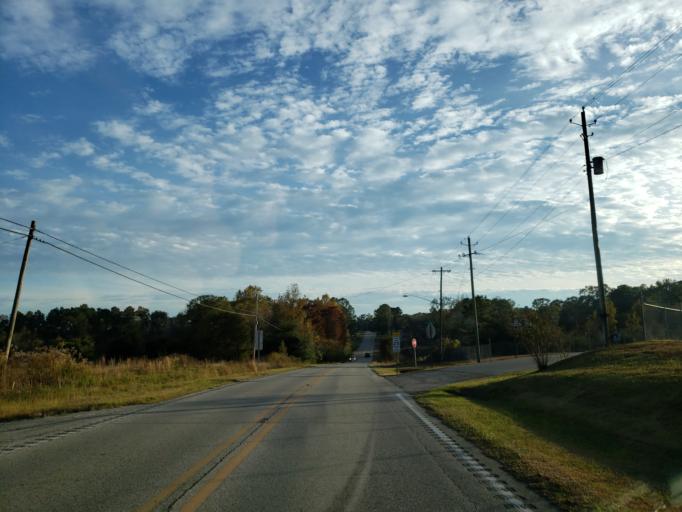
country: US
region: Mississippi
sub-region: Lamar County
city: Purvis
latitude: 31.1369
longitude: -89.4055
